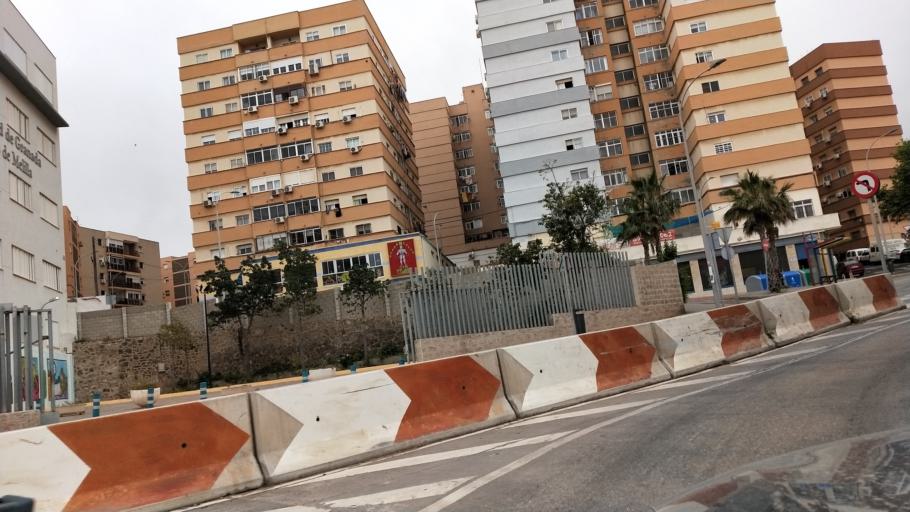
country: ES
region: Melilla
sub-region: Melilla
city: Melilla
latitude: 35.2900
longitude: -2.9533
